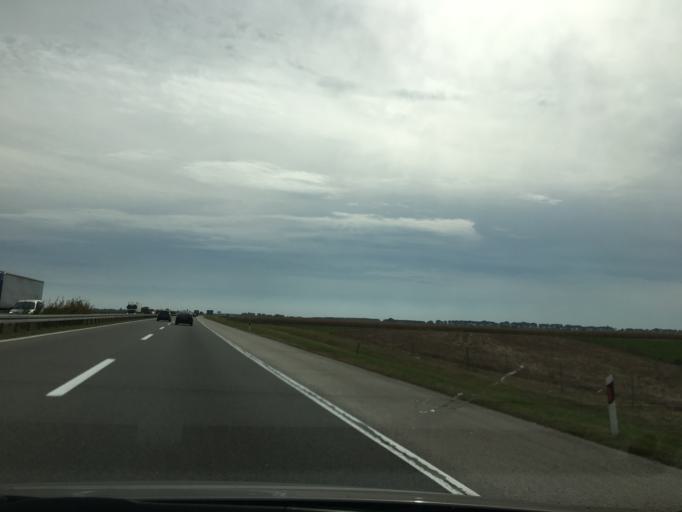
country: RS
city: Novi Karlovci
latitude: 45.0440
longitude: 20.1789
